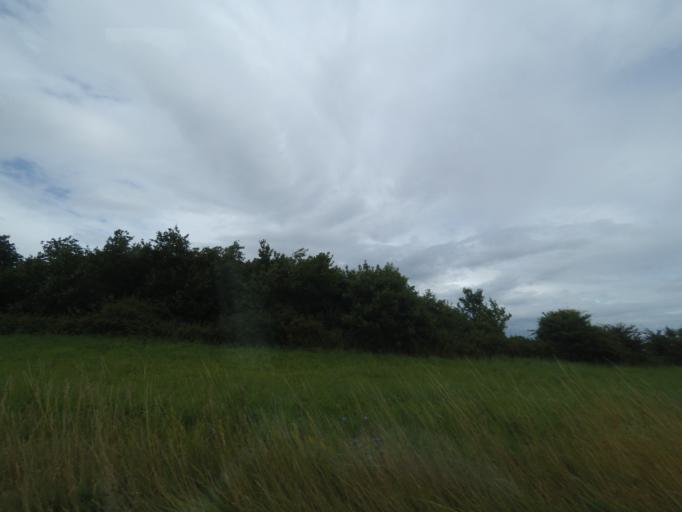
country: DK
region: South Denmark
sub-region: Nordfyns Kommune
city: Sonderso
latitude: 55.4954
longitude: 10.2753
